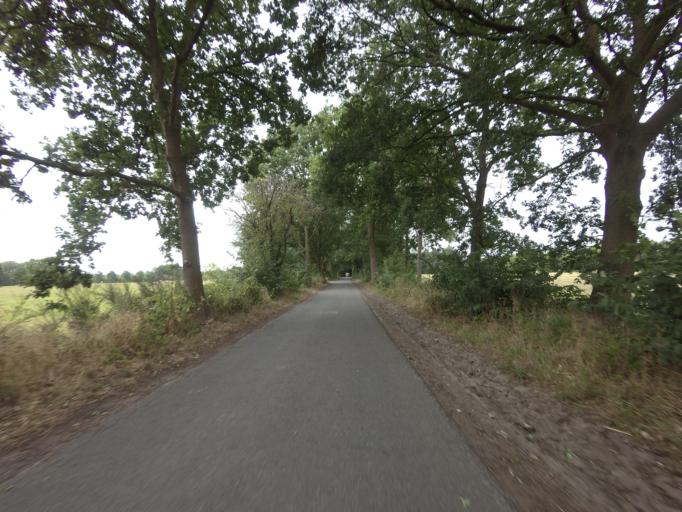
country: NL
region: Utrecht
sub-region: Gemeente De Bilt
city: De Bilt
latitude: 52.1235
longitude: 5.1655
